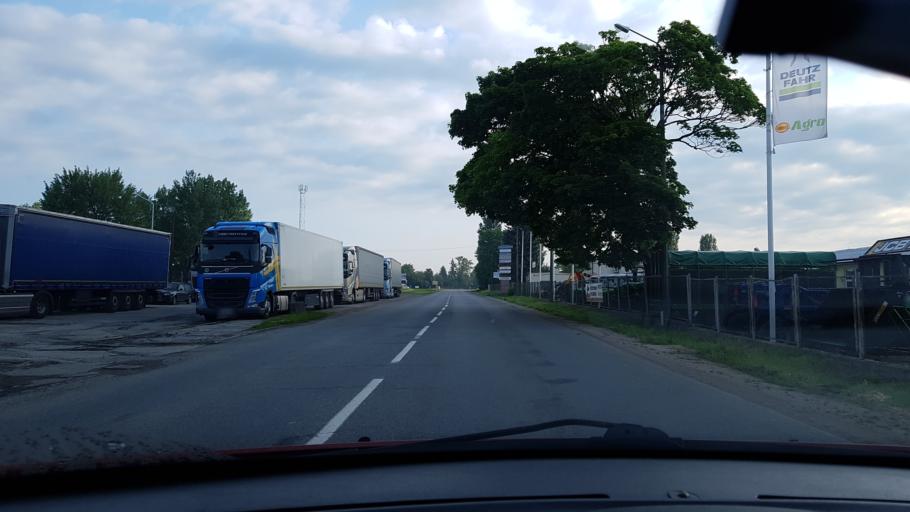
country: PL
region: Lower Silesian Voivodeship
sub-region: Powiat zabkowicki
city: Zabkowice Slaskie
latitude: 50.6002
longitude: 16.8194
